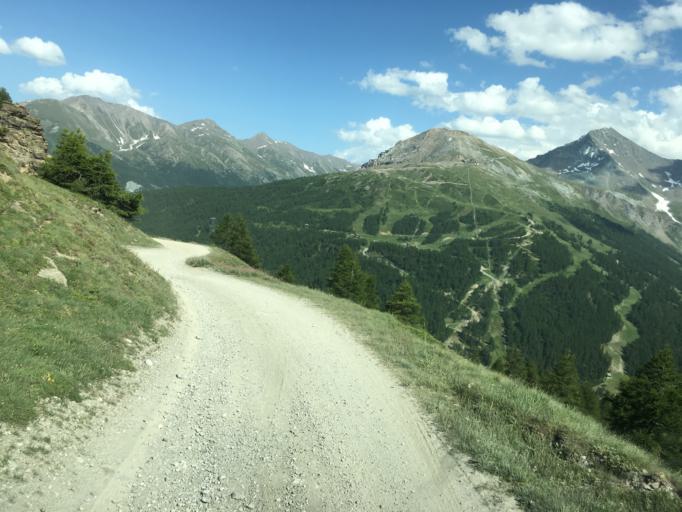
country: IT
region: Piedmont
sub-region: Provincia di Torino
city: Sestriere
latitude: 44.9773
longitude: 6.8786
